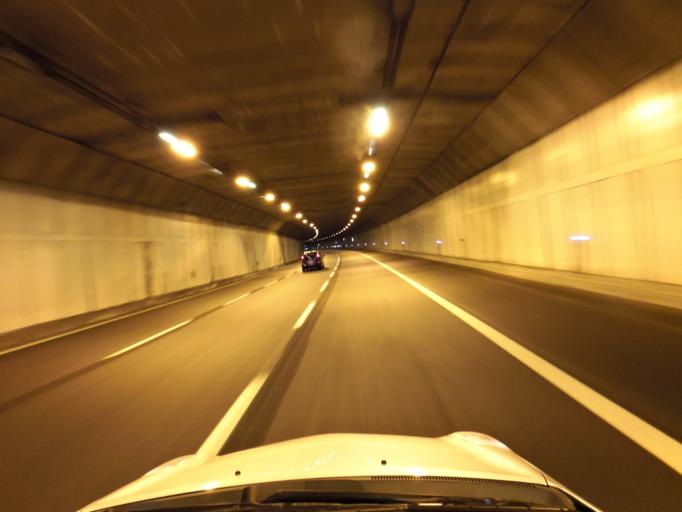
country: IT
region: Emilia-Romagna
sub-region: Provincia di Bologna
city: Vado
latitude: 44.2981
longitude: 11.2359
